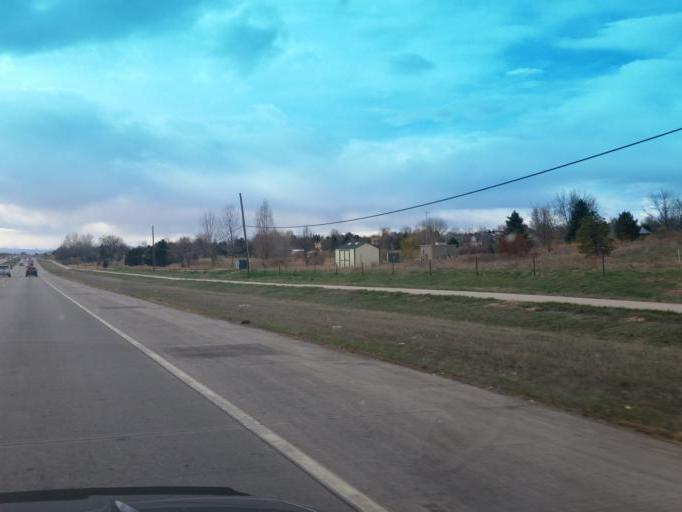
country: US
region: Colorado
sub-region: Weld County
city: Greeley
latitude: 40.3922
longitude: -104.7680
